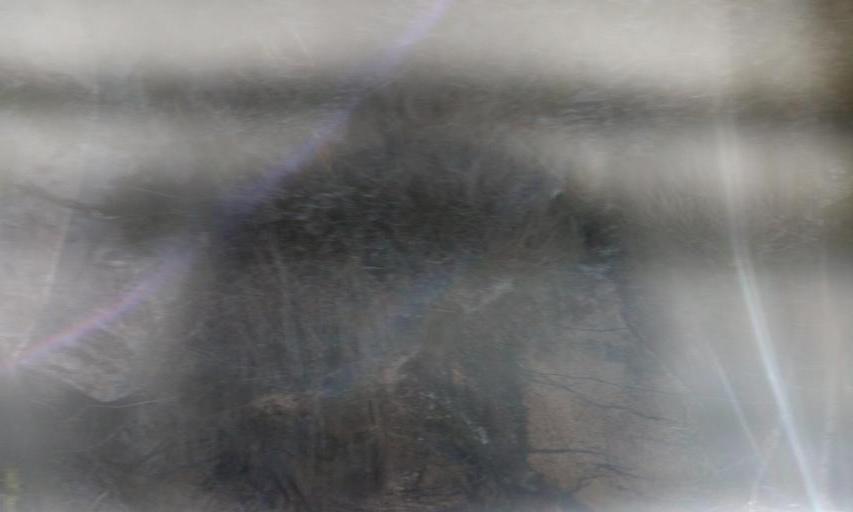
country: PT
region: Guarda
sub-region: Manteigas
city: Manteigas
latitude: 40.4840
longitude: -7.5166
